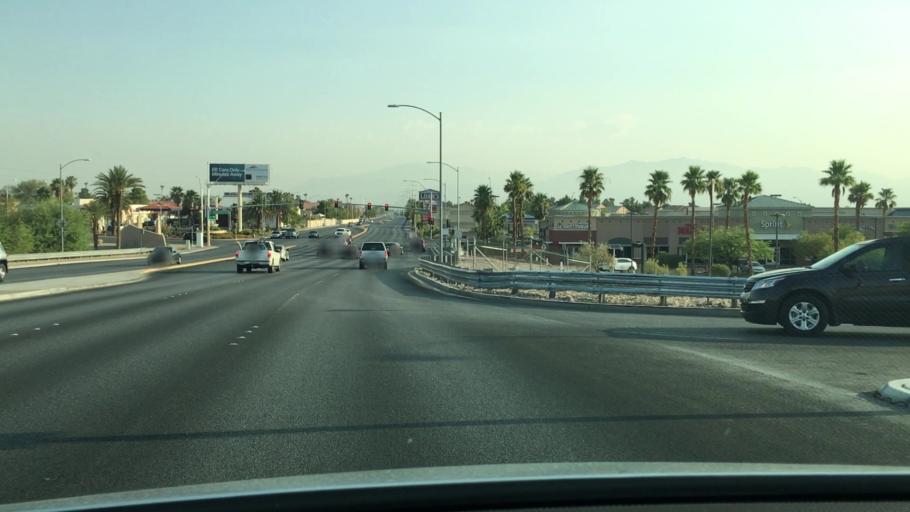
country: US
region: Nevada
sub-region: Clark County
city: Spring Valley
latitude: 36.1800
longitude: -115.2598
